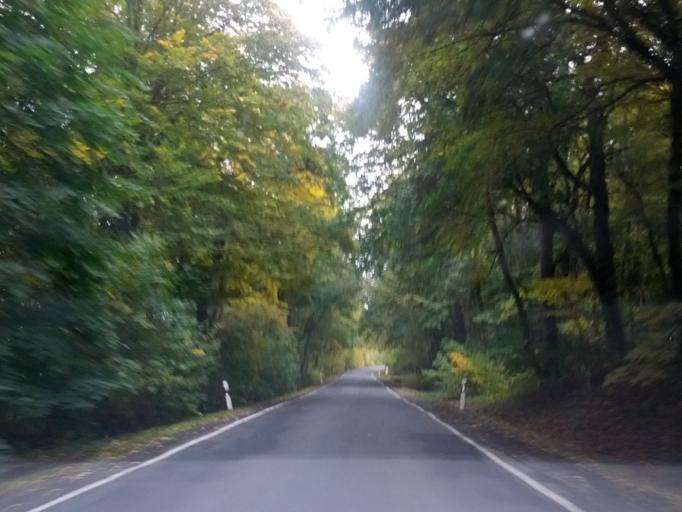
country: DE
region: Thuringia
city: Klettbach
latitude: 50.9381
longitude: 11.1702
